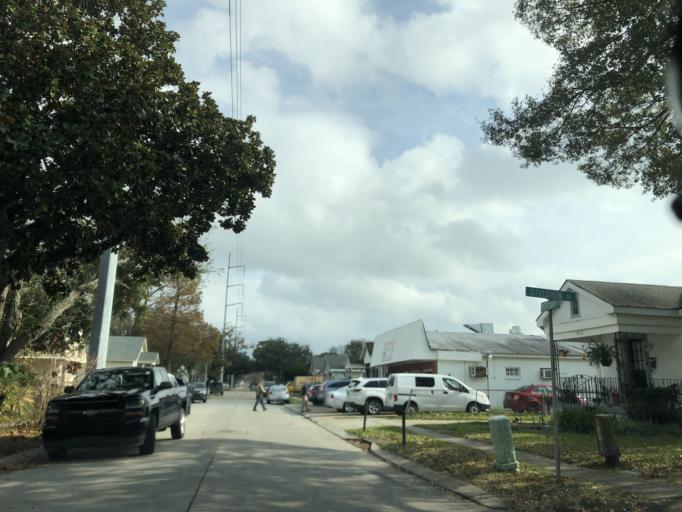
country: US
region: Louisiana
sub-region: Jefferson Parish
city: Metairie Terrace
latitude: 29.9768
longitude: -90.1653
